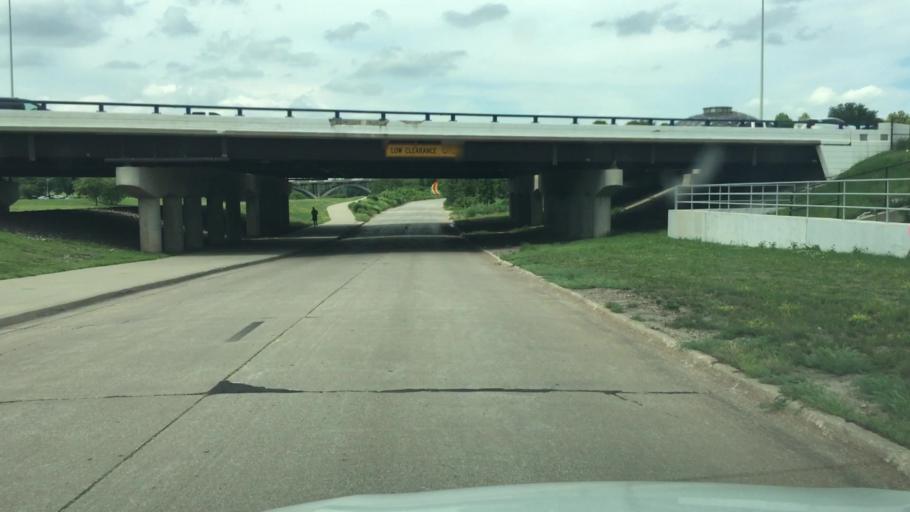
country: US
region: Iowa
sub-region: Polk County
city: Des Moines
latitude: 41.5950
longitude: -93.6160
